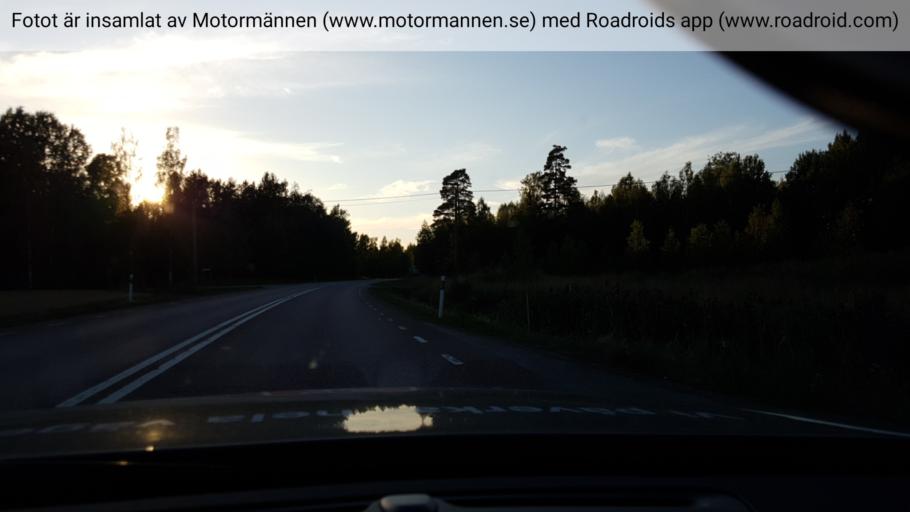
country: SE
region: OErebro
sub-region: Karlskoga Kommun
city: Karlskoga
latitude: 59.3987
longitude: 14.4376
